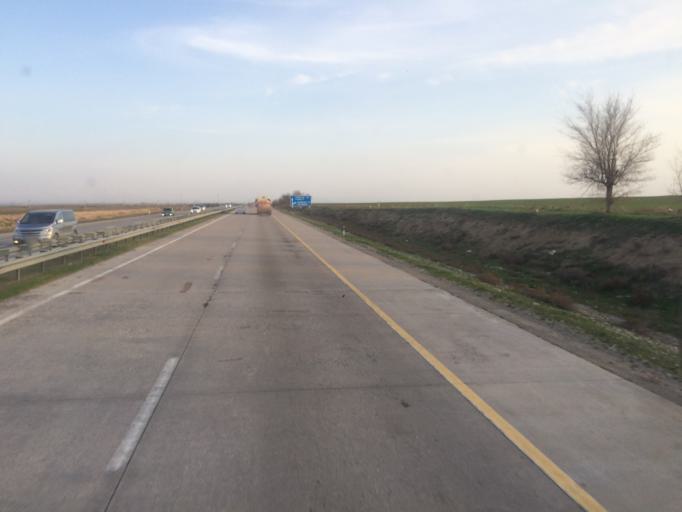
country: KZ
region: Ongtustik Qazaqstan
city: Temirlanovka
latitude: 42.5385
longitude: 69.3319
